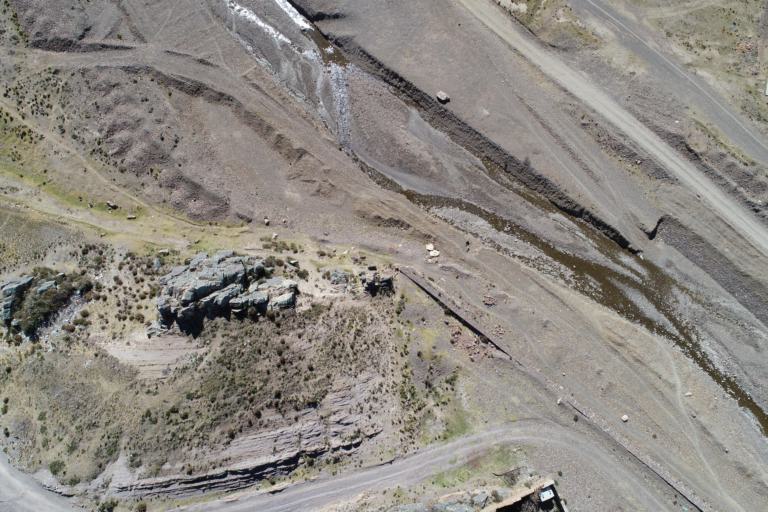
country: BO
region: La Paz
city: Achacachi
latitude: -15.8960
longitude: -68.9029
